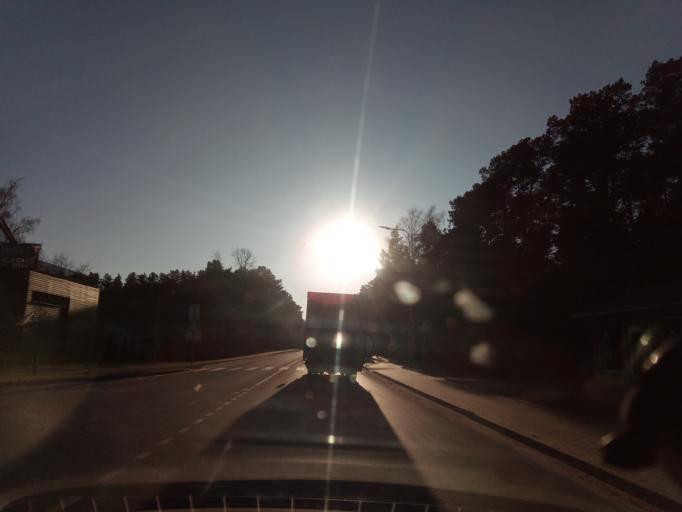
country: LT
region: Alytaus apskritis
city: Druskininkai
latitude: 54.0207
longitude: 24.0008
